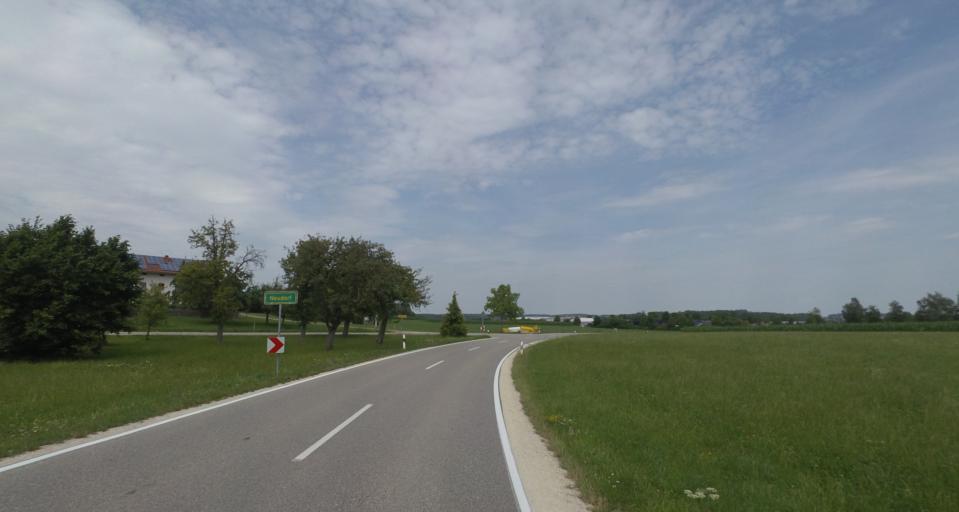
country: DE
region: Bavaria
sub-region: Upper Bavaria
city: Traunreut
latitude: 47.9555
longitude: 12.5570
